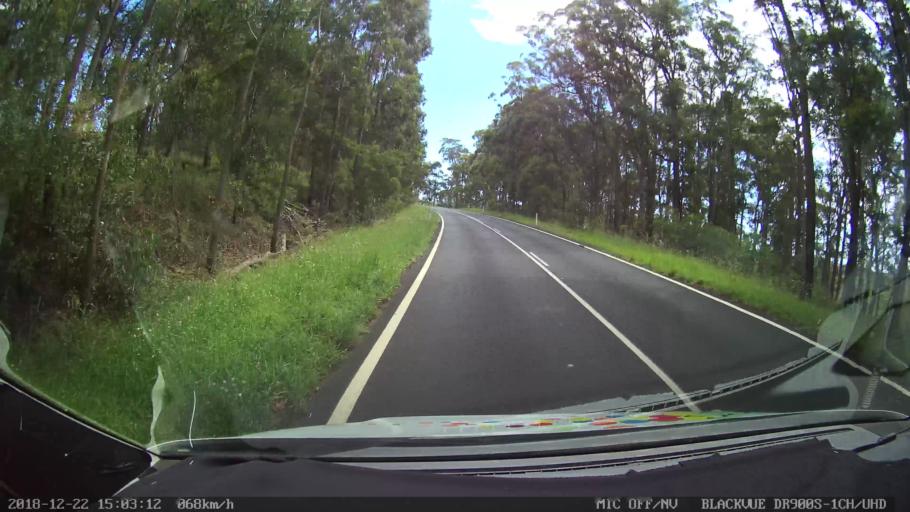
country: AU
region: New South Wales
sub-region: Bellingen
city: Dorrigo
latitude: -30.2626
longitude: 152.4425
